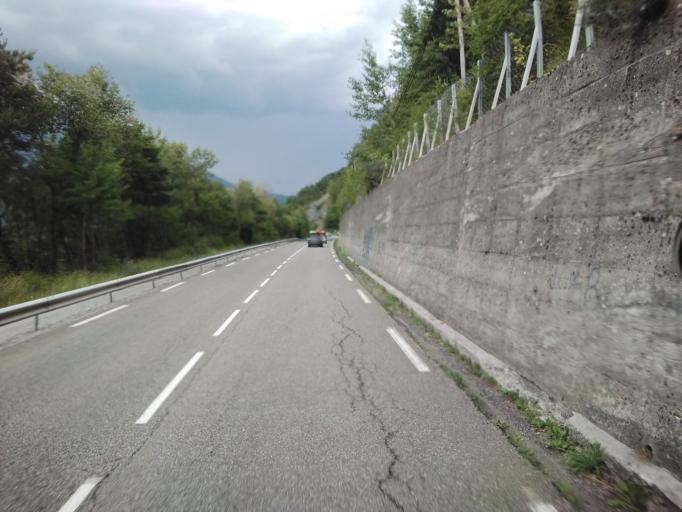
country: FR
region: Provence-Alpes-Cote d'Azur
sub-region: Departement des Hautes-Alpes
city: Embrun
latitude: 44.5205
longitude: 6.3918
